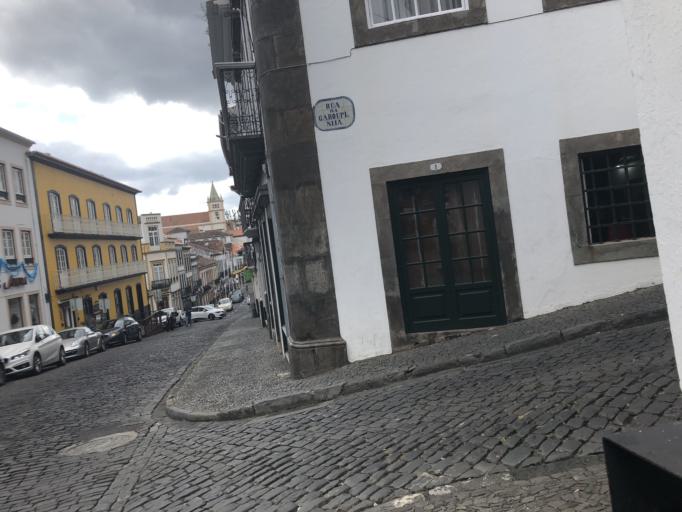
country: PT
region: Azores
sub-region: Angra do Heroismo
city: Angra do Heroismo
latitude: 38.6558
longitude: -27.2172
